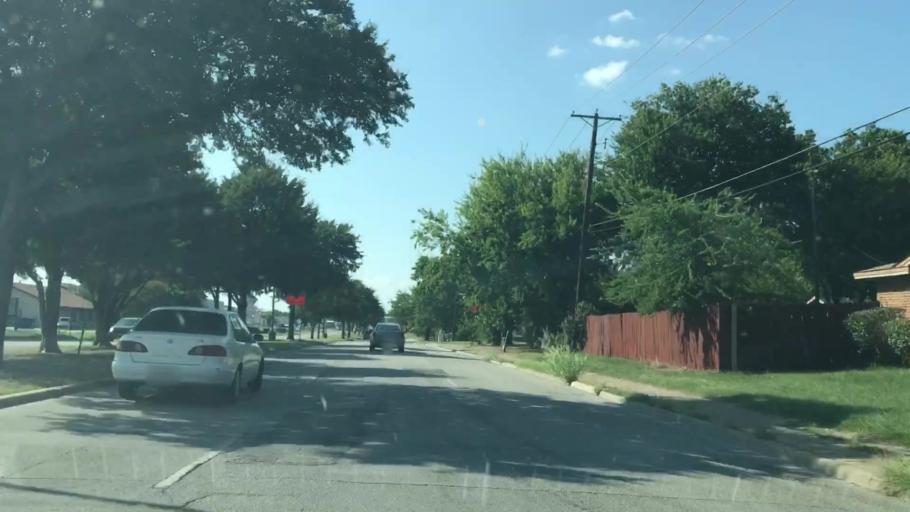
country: US
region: Texas
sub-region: Dallas County
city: Mesquite
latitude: 32.8279
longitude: -96.6512
